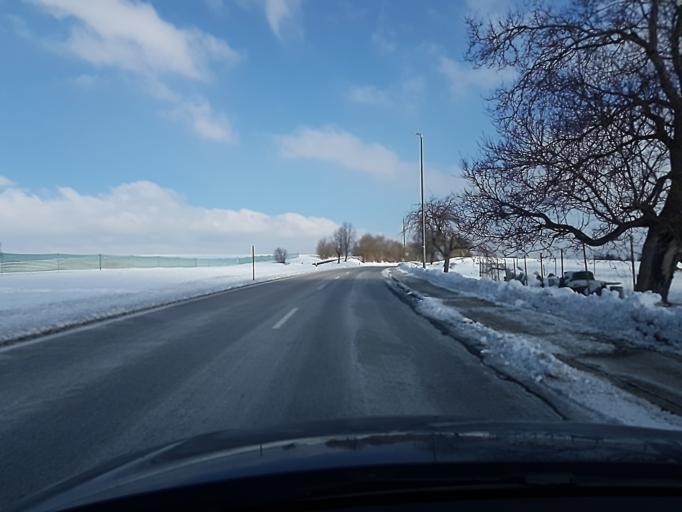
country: DE
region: Baden-Wuerttemberg
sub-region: Freiburg Region
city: Oberndorf
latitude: 48.2839
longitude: 8.5436
